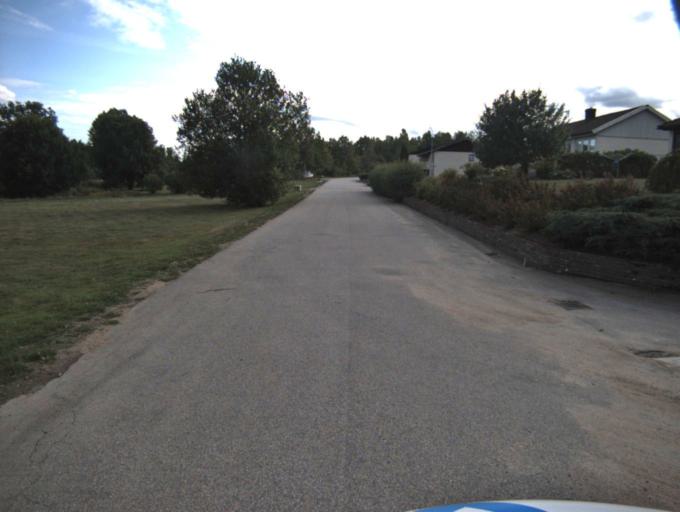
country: SE
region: Vaestra Goetaland
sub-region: Ulricehamns Kommun
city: Ulricehamn
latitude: 57.6830
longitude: 13.3781
